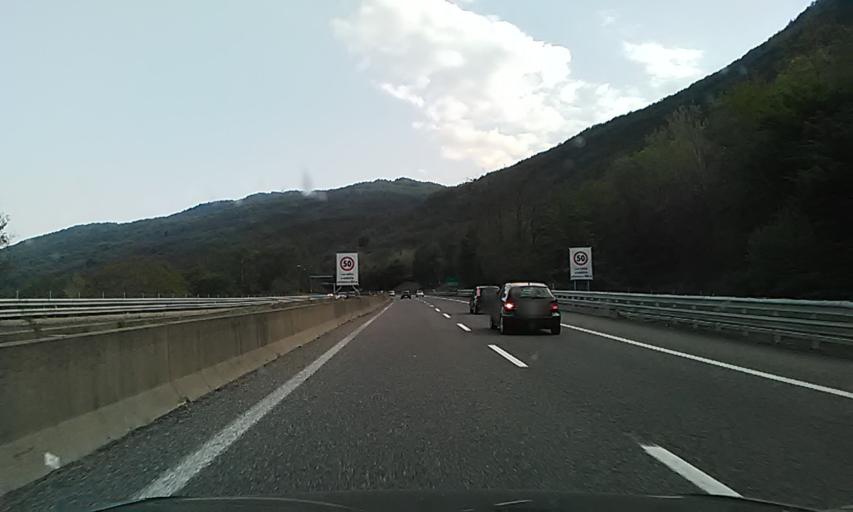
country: IT
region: Piedmont
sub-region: Provincia Verbano-Cusio-Ossola
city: Baveno
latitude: 45.9181
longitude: 8.4850
